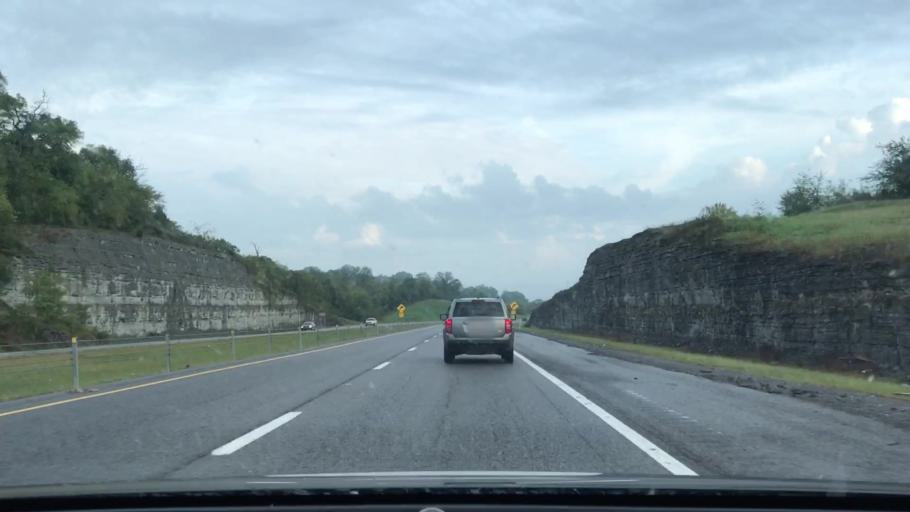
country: US
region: Tennessee
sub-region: Sumner County
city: Shackle Island
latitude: 36.3393
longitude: -86.5496
